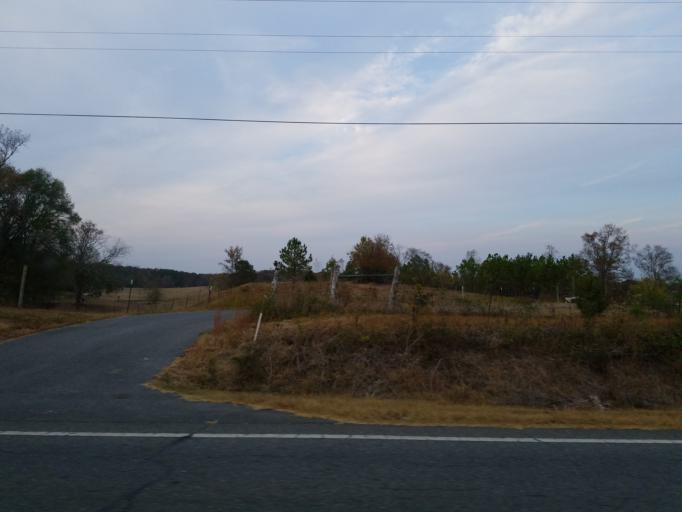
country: US
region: Georgia
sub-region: Gordon County
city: Calhoun
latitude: 34.6012
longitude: -84.8417
